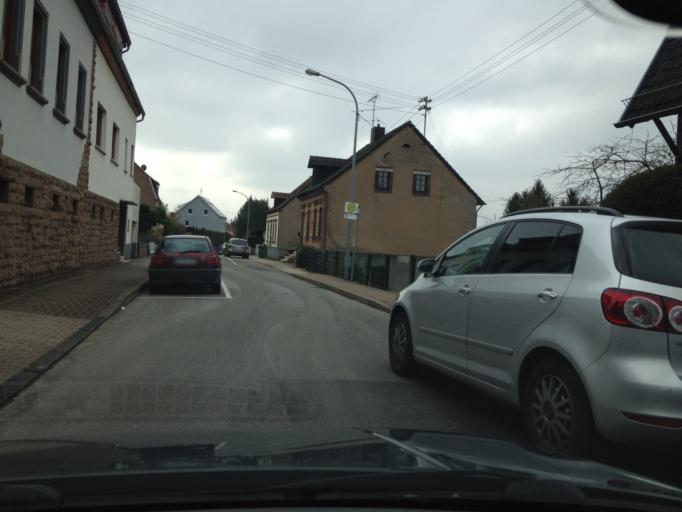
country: DE
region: Saarland
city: Ottweiler
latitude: 49.3985
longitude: 7.1716
